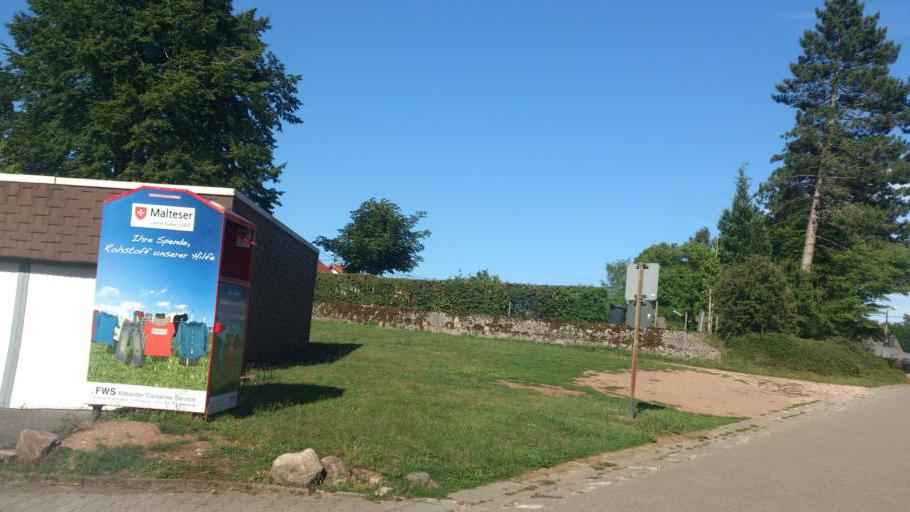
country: DE
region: Saarland
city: Oberthal
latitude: 49.5495
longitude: 7.0599
